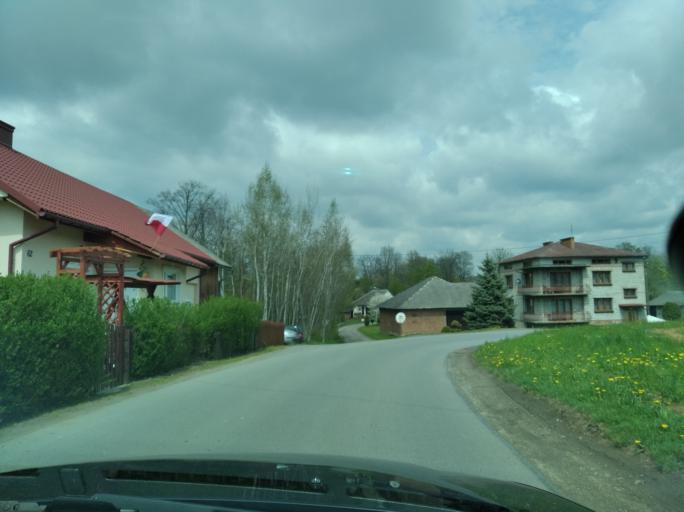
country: PL
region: Subcarpathian Voivodeship
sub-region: Powiat brzozowski
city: Haczow
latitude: 49.6739
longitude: 21.8929
